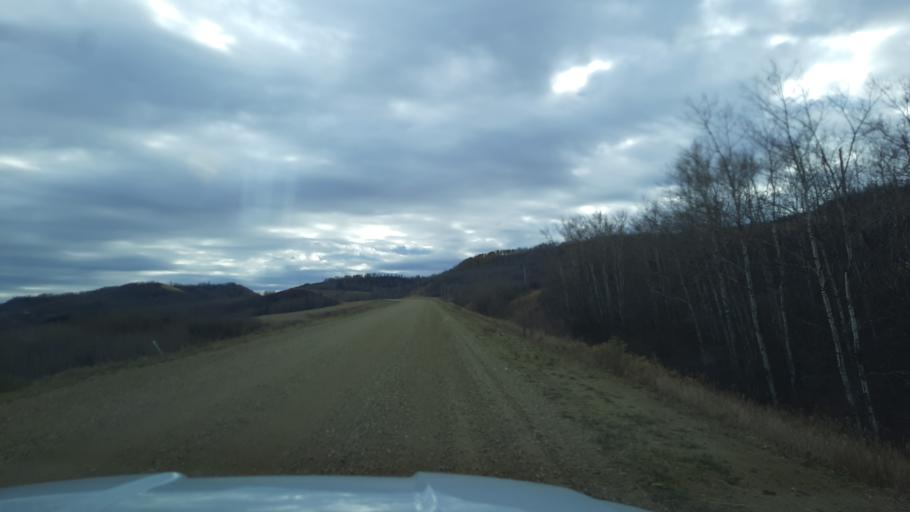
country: CA
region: Saskatchewan
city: Pilot Butte
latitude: 50.7739
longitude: -104.2821
